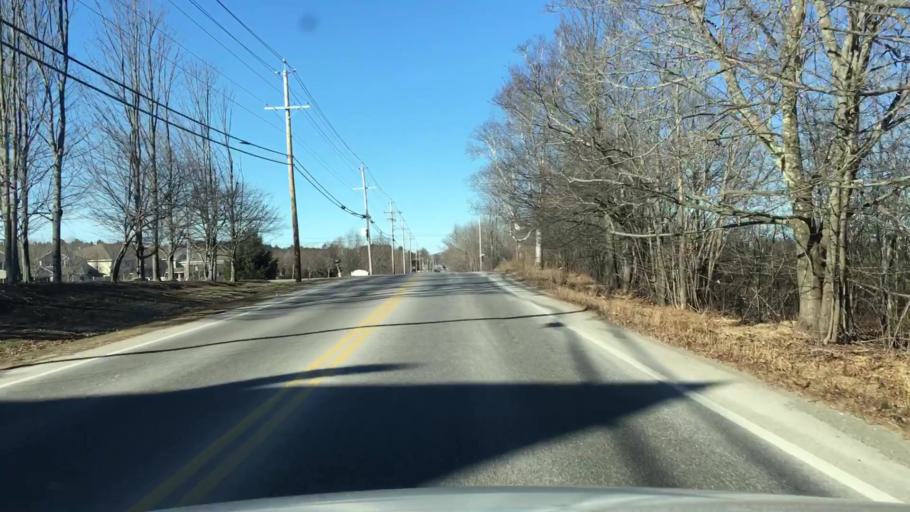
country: US
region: Maine
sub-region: Penobscot County
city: Bangor
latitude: 44.8209
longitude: -68.8045
